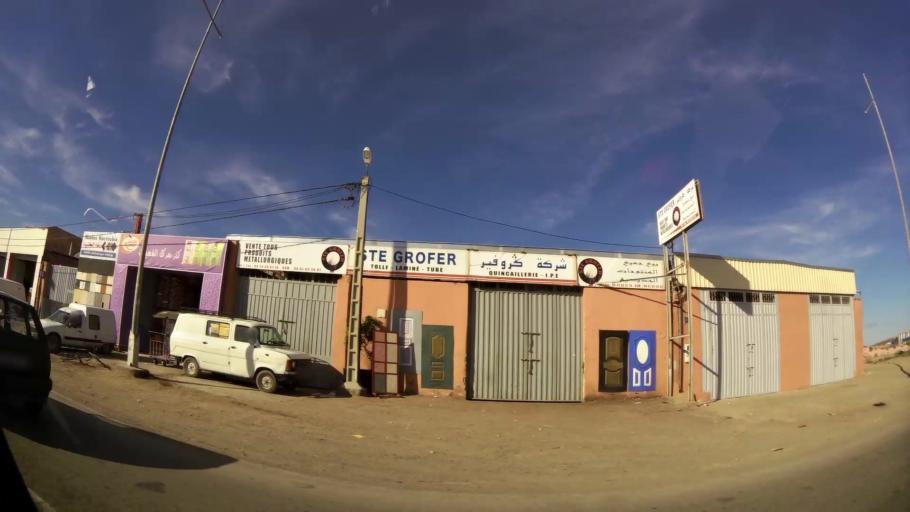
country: MA
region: Marrakech-Tensift-Al Haouz
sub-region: Marrakech
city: Marrakesh
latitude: 31.7149
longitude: -8.0754
